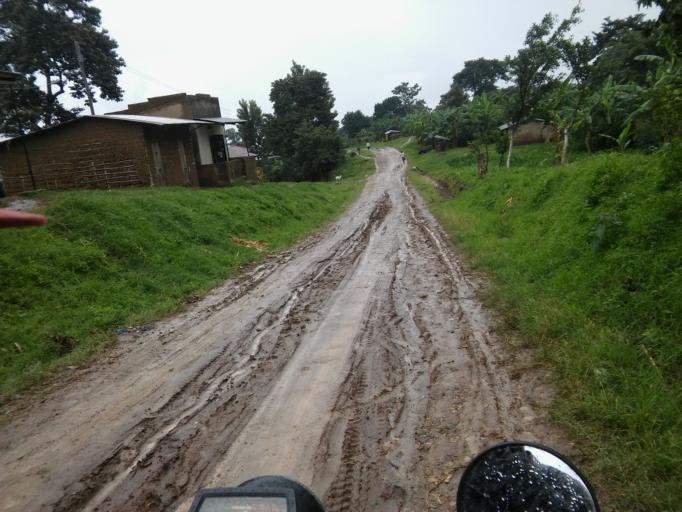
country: UG
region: Eastern Region
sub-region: Mbale District
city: Mbale
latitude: 1.0103
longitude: 34.2348
